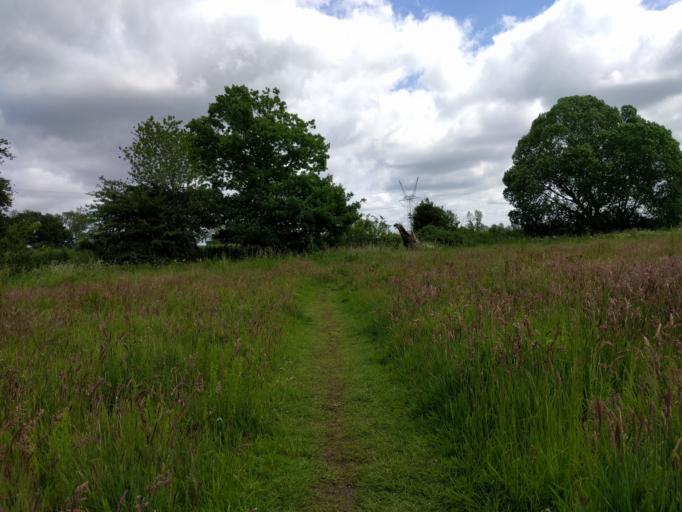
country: DK
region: South Denmark
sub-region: Odense Kommune
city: Bullerup
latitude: 55.4311
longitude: 10.4941
